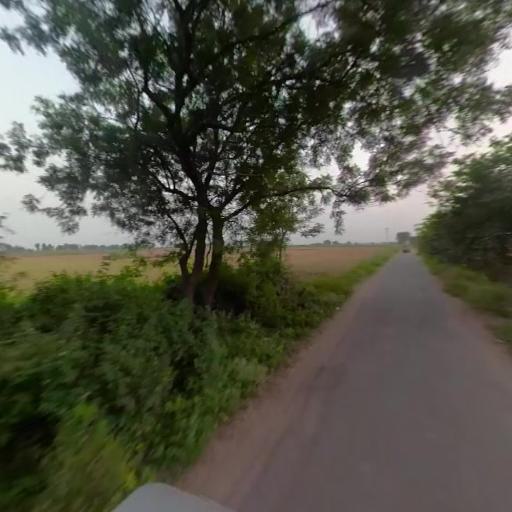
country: IN
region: Telangana
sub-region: Nalgonda
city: Suriapet
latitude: 17.1129
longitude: 79.5288
